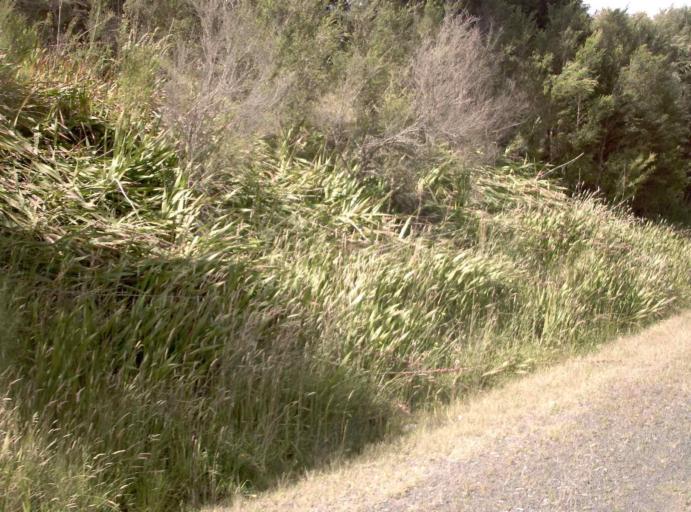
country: AU
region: Victoria
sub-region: Latrobe
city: Morwell
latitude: -38.1581
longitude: 146.4213
